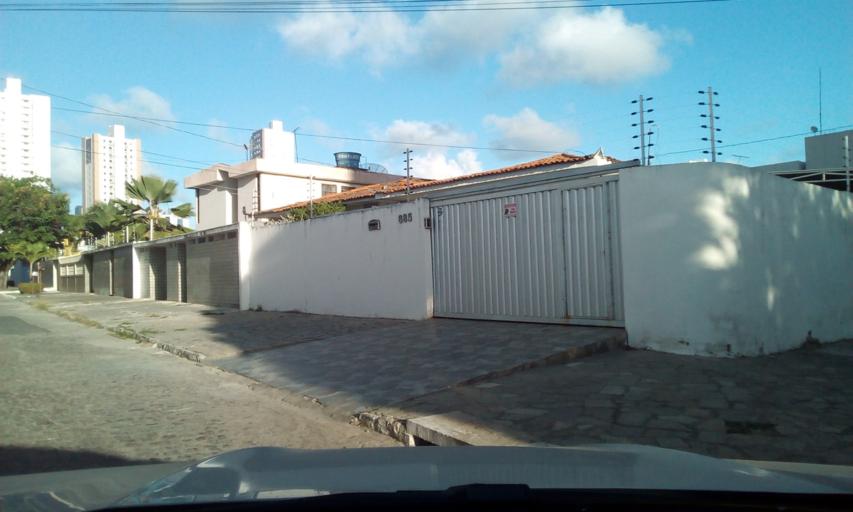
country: BR
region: Paraiba
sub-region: Joao Pessoa
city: Joao Pessoa
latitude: -7.1030
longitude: -34.8419
